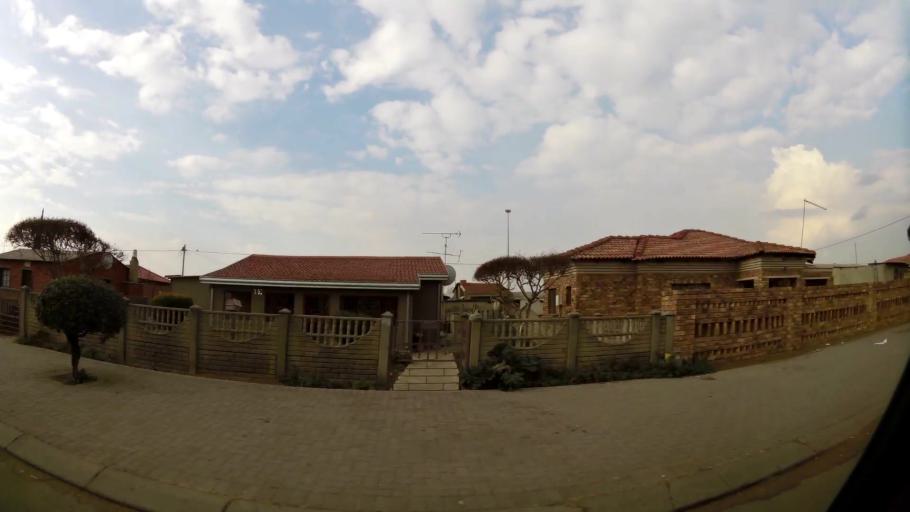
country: ZA
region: Gauteng
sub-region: Sedibeng District Municipality
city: Vanderbijlpark
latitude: -26.6860
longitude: 27.8687
